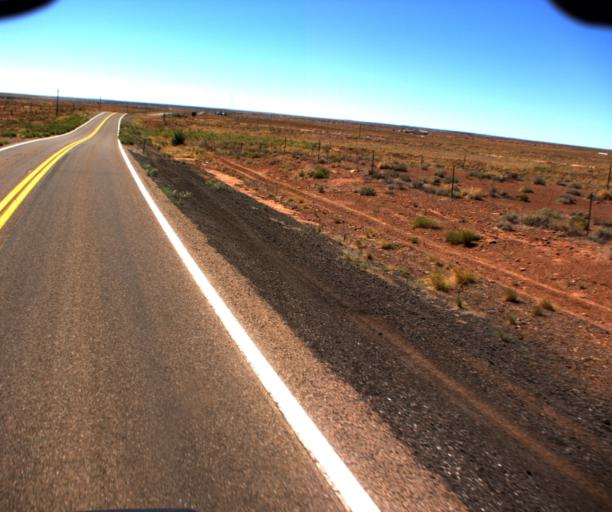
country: US
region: Arizona
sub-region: Navajo County
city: Winslow
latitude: 34.9953
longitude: -110.6718
